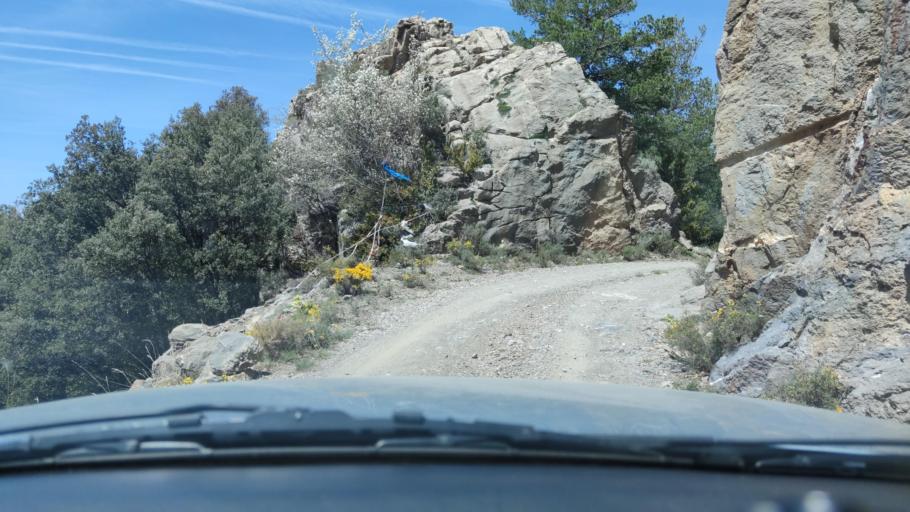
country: ES
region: Catalonia
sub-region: Provincia de Lleida
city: Sort
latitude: 42.3090
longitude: 1.1521
